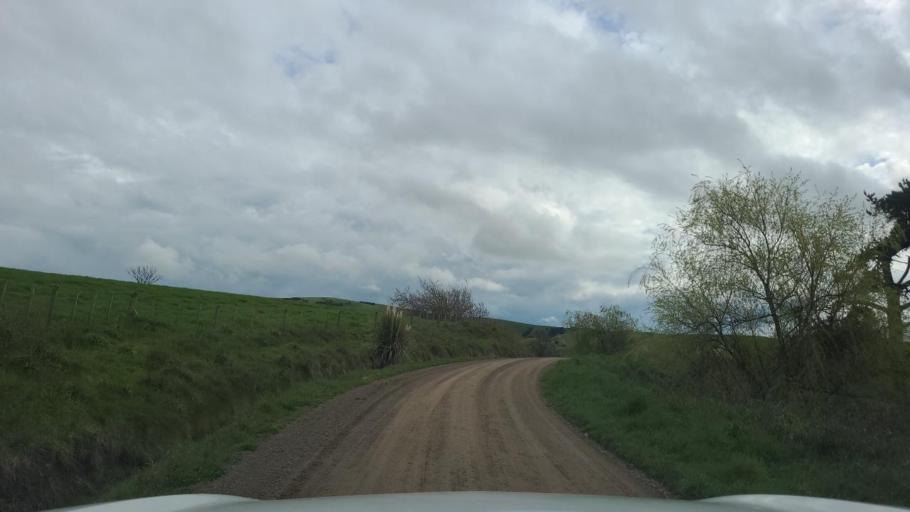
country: NZ
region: Wellington
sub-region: Masterton District
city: Masterton
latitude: -41.1094
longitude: 175.5481
